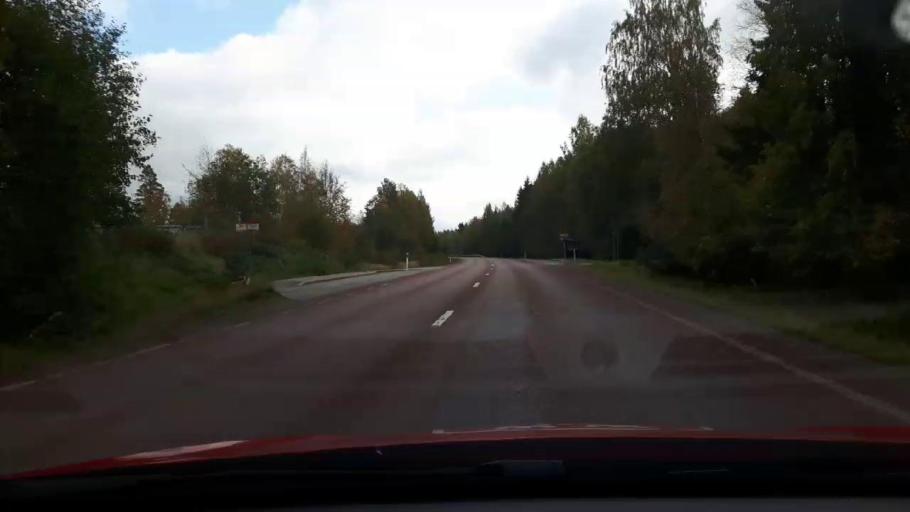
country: SE
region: Gaevleborg
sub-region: Ljusdals Kommun
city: Jaervsoe
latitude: 61.6386
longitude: 16.2404
